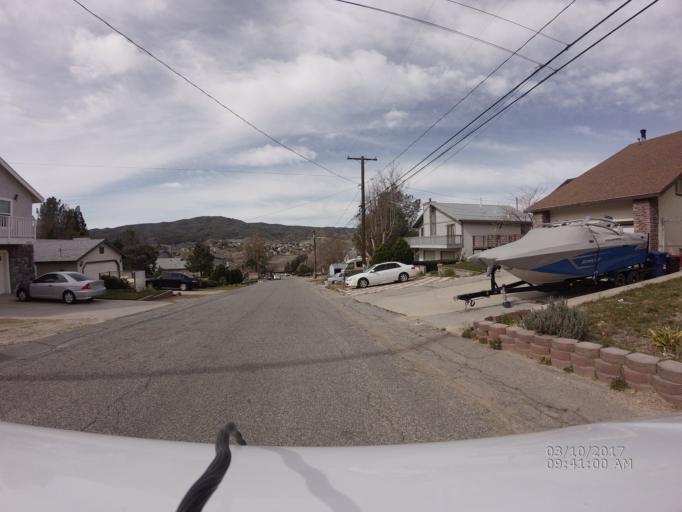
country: US
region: California
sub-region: Los Angeles County
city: Green Valley
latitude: 34.6679
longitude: -118.3879
